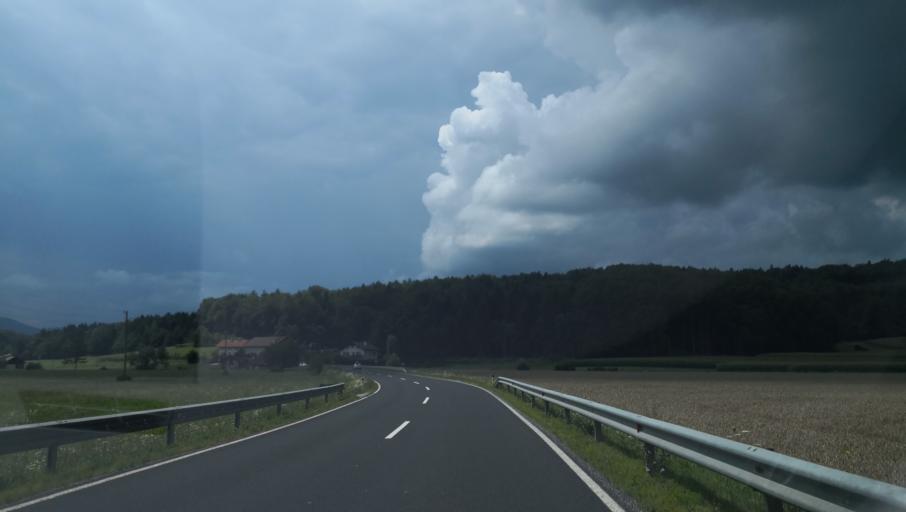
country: SI
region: Ivancna Gorica
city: Ivancna Gorica
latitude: 45.9170
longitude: 14.8047
